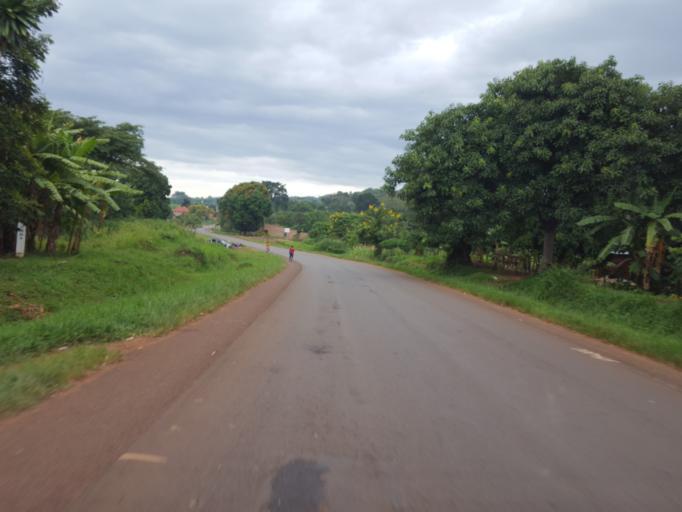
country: UG
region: Central Region
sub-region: Kiboga District
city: Kiboga
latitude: 0.8705
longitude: 31.8546
